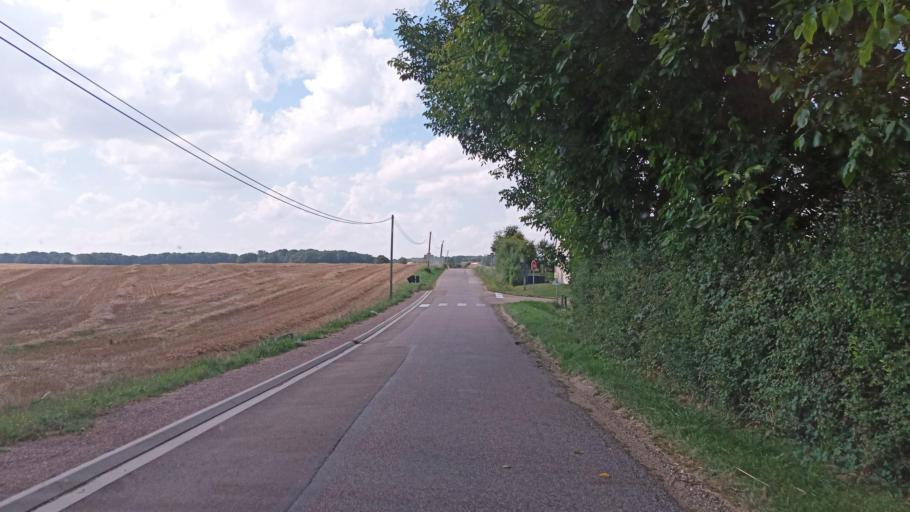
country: FR
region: Bourgogne
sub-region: Departement de l'Yonne
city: Egriselles-le-Bocage
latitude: 48.0243
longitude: 3.1745
